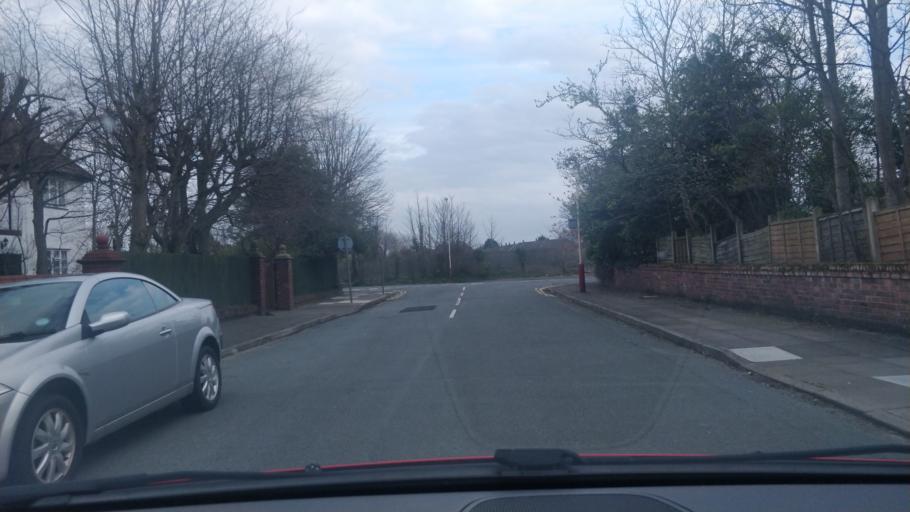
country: GB
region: England
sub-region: Sefton
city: Southport
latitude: 53.6059
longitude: -3.0402
